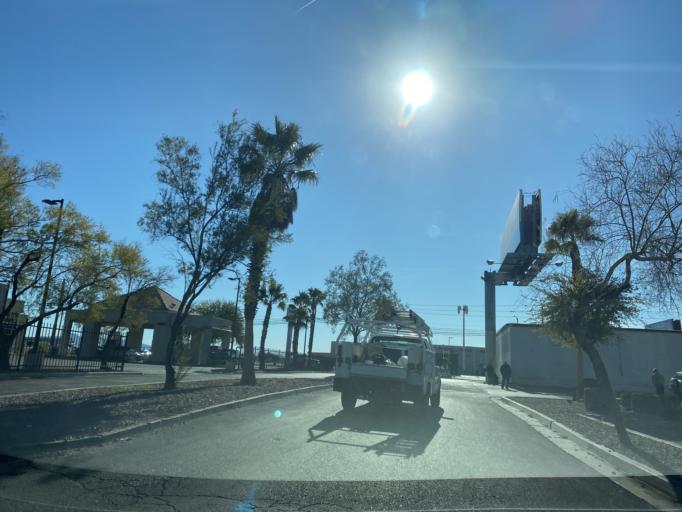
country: US
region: Nevada
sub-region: Clark County
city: Spring Valley
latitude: 36.1017
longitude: -115.2069
